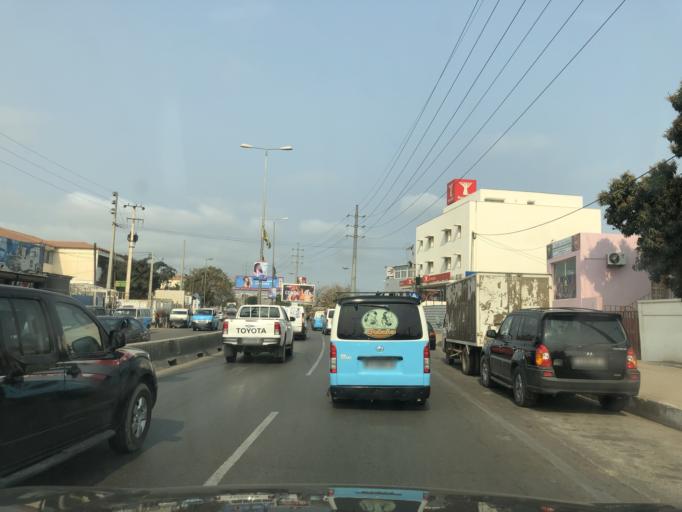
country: AO
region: Luanda
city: Luanda
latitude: -8.8938
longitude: 13.1832
